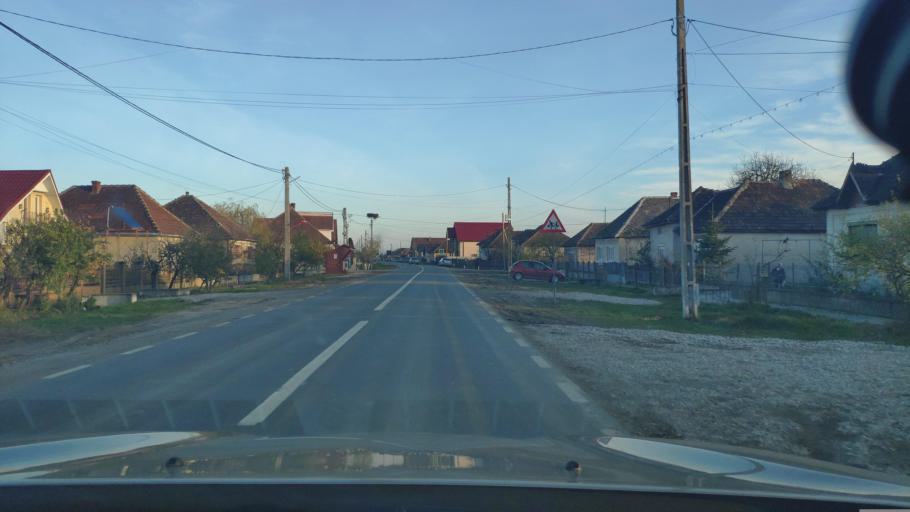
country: RO
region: Satu Mare
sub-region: Comuna Mediesu Aurit
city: Potau
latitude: 47.7747
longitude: 23.1008
